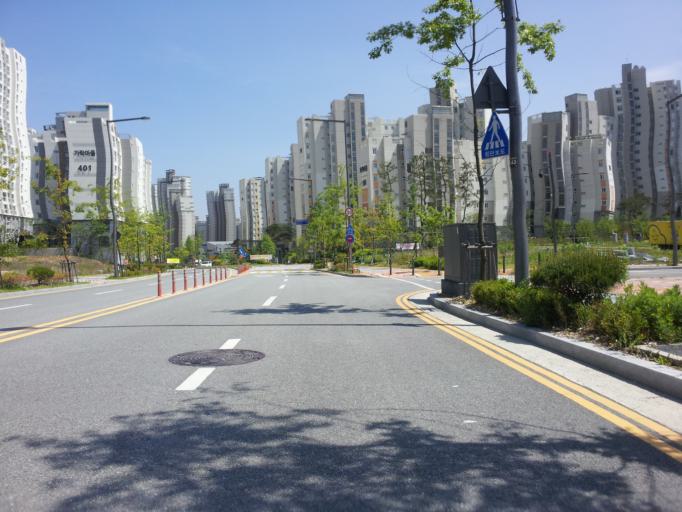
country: KR
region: Chungcheongnam-do
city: Gongju
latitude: 36.5082
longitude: 127.2349
